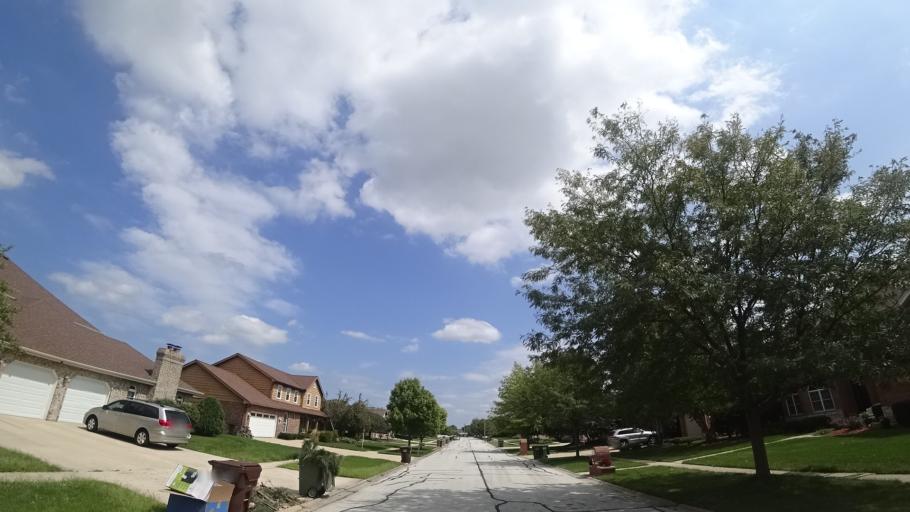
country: US
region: Illinois
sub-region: Cook County
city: Orland Hills
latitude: 41.5661
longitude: -87.8166
